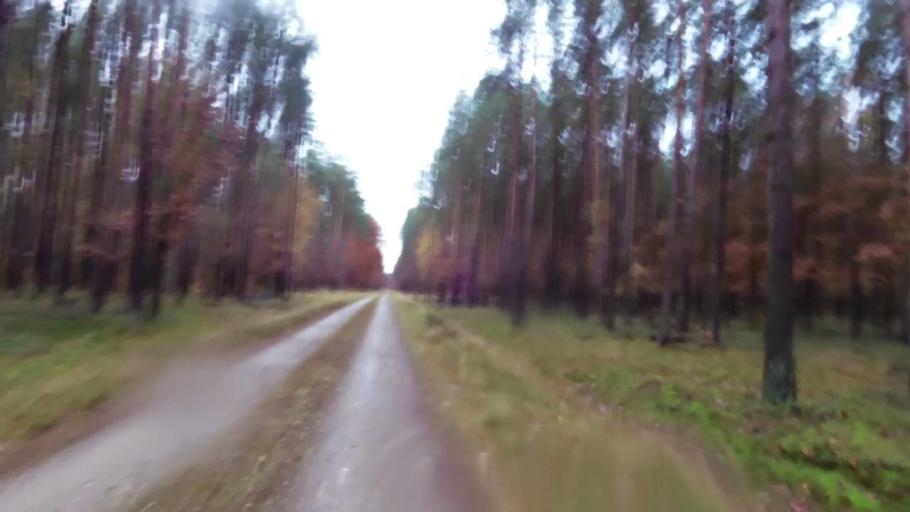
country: PL
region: West Pomeranian Voivodeship
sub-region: Powiat goleniowski
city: Stepnica
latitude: 53.6440
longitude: 14.7032
